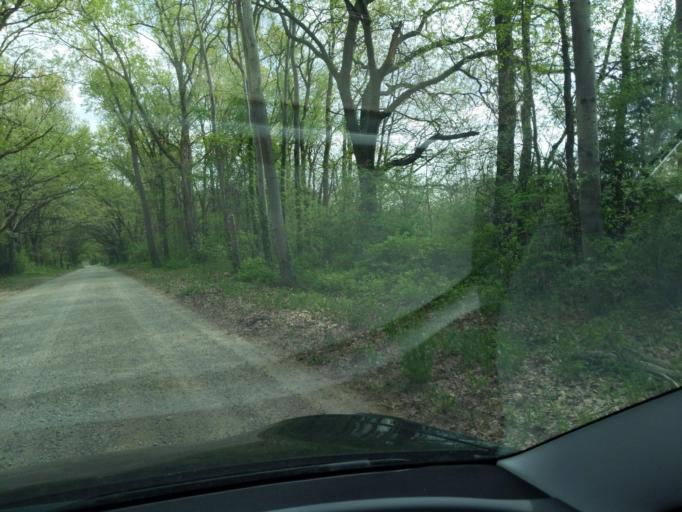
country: US
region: Michigan
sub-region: Washtenaw County
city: Chelsea
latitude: 42.4166
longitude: -84.0611
